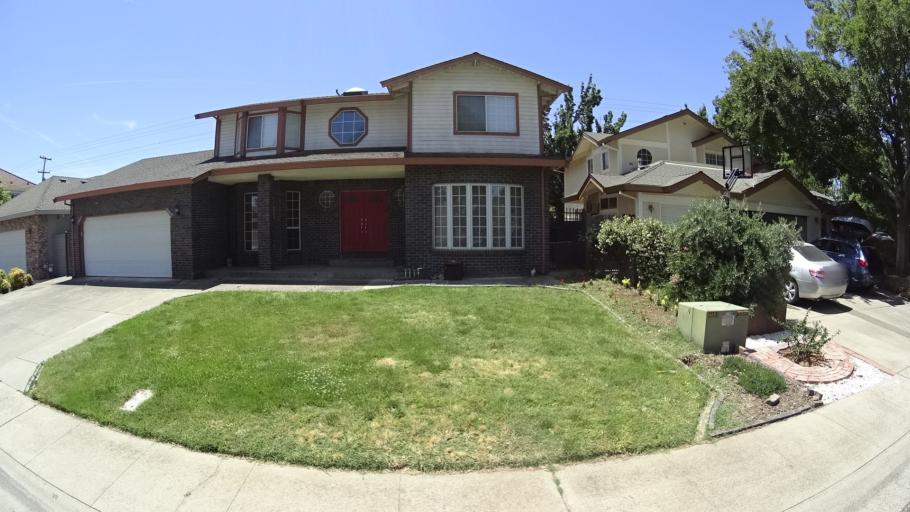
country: US
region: California
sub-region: Yolo County
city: West Sacramento
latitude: 38.5235
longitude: -121.5162
